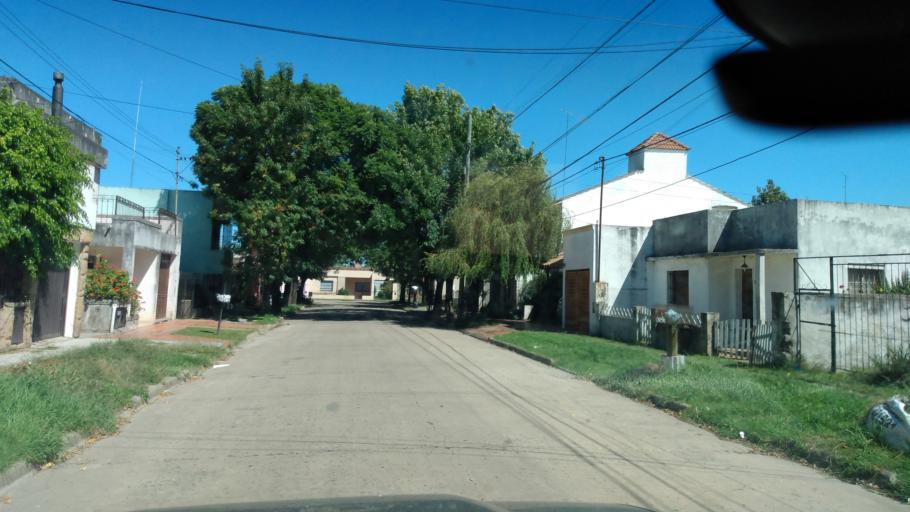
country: AR
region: Buenos Aires
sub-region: Partido de Lujan
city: Lujan
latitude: -34.5789
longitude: -59.1115
